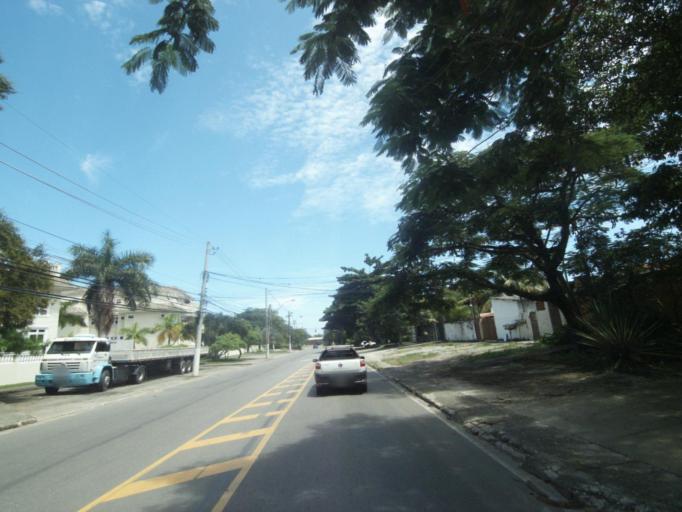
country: BR
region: Rio de Janeiro
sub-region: Niteroi
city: Niteroi
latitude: -22.9520
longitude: -43.0255
